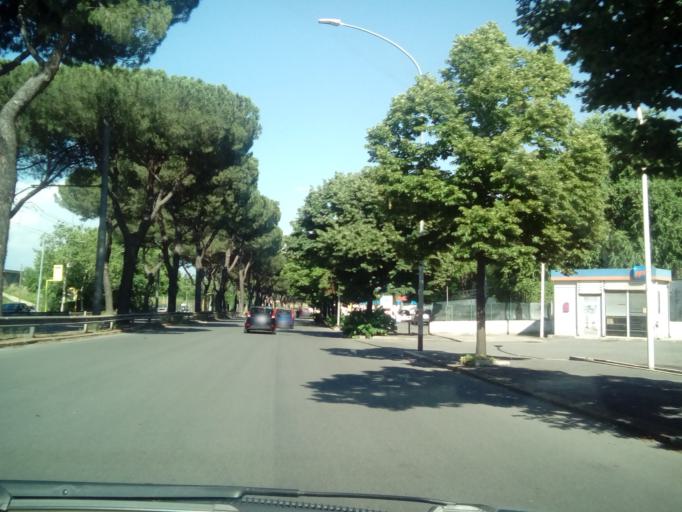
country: IT
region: Latium
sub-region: Citta metropolitana di Roma Capitale
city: Rome
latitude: 41.8950
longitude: 12.5696
